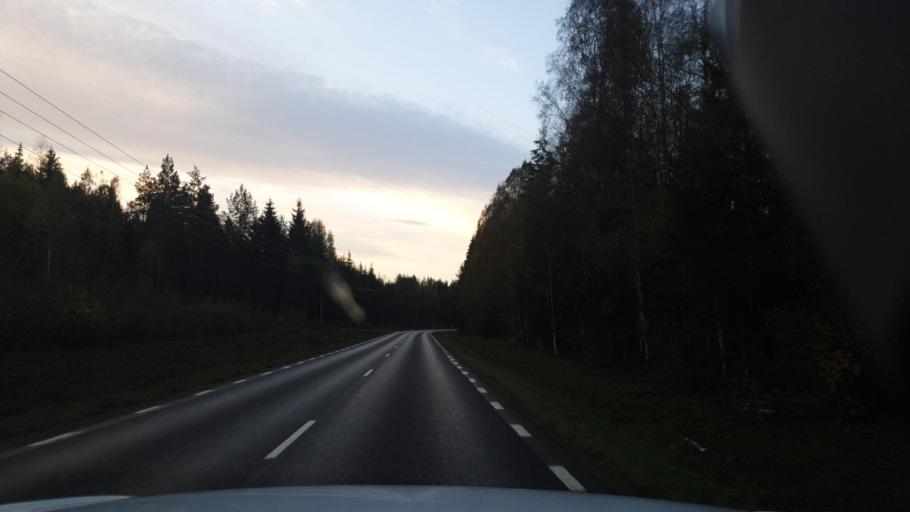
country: SE
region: Vaermland
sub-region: Arvika Kommun
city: Arvika
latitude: 59.7249
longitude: 12.5669
